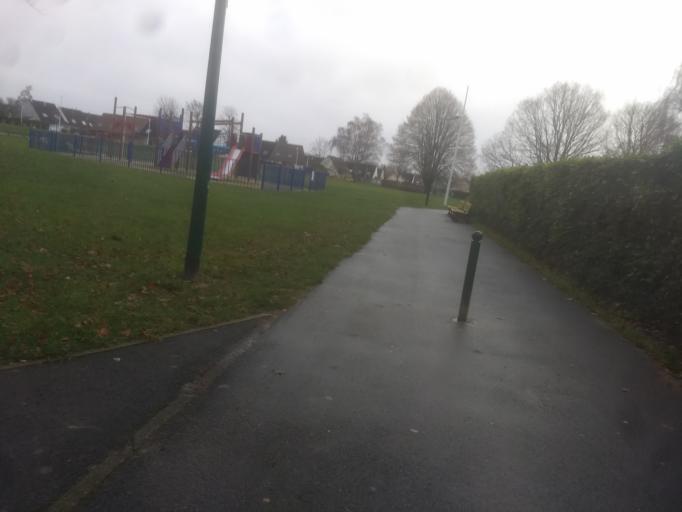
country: FR
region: Nord-Pas-de-Calais
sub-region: Departement du Pas-de-Calais
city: Saint-Nicolas
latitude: 50.3051
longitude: 2.7879
